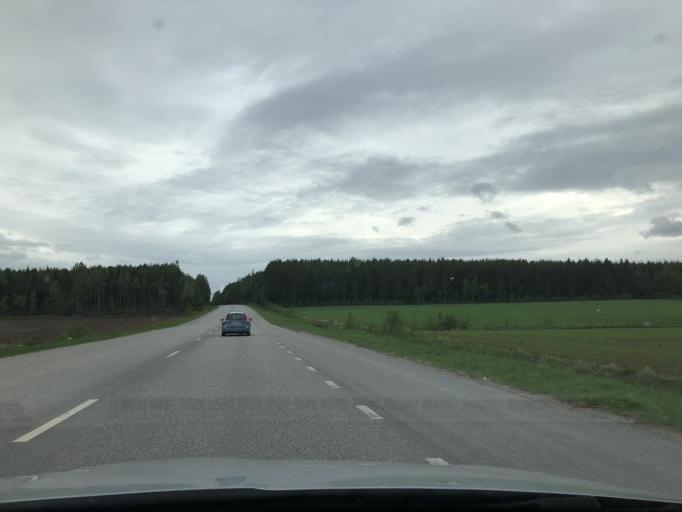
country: SE
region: Norrbotten
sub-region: Pitea Kommun
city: Norrfjarden
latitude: 65.3707
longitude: 21.4184
